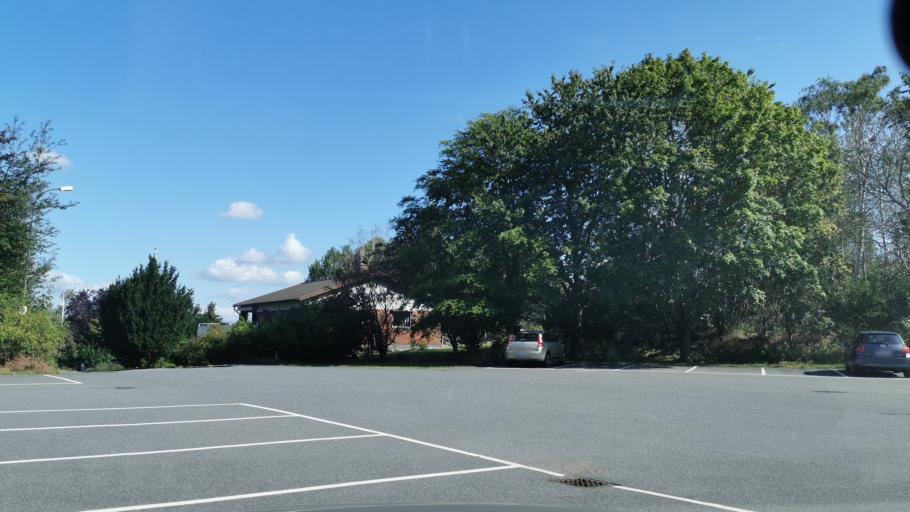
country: SE
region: Vaestra Goetaland
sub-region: Molndal
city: Moelndal
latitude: 57.6712
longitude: 11.9976
